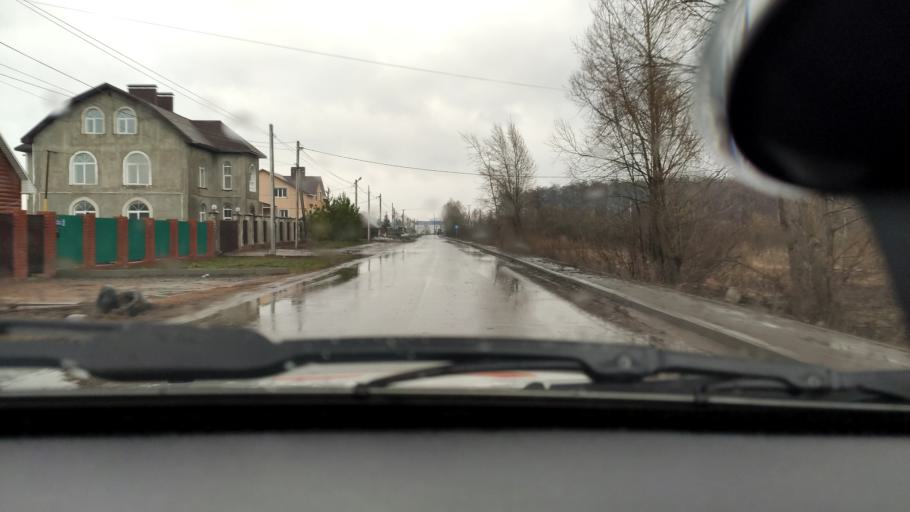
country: RU
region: Bashkortostan
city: Mikhaylovka
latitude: 54.7847
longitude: 55.8163
